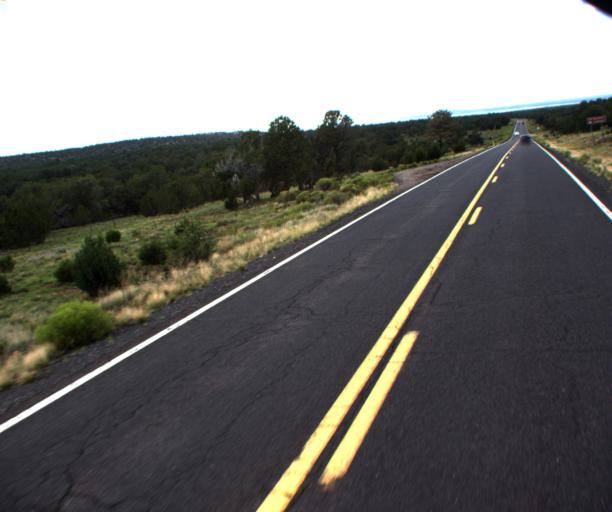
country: US
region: Arizona
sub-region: Coconino County
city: Parks
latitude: 35.5350
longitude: -111.8515
